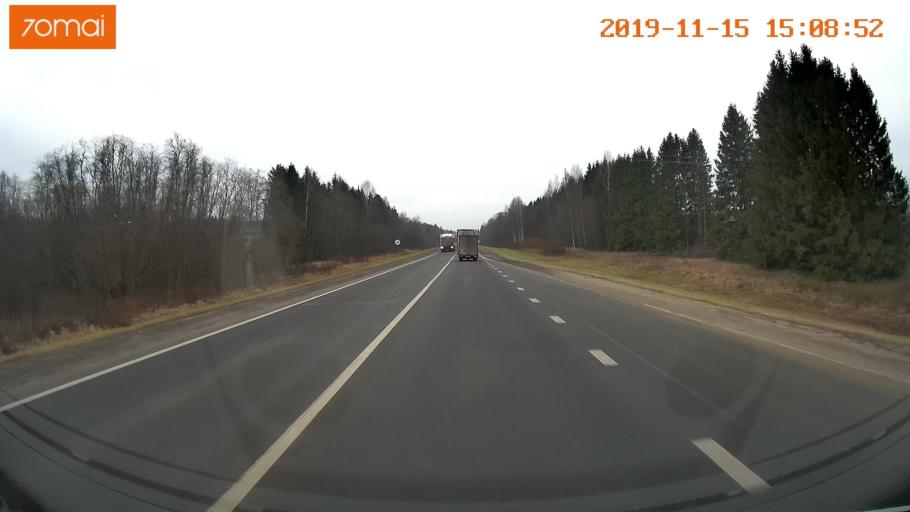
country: RU
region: Jaroslavl
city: Prechistoye
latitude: 58.3649
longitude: 40.2711
